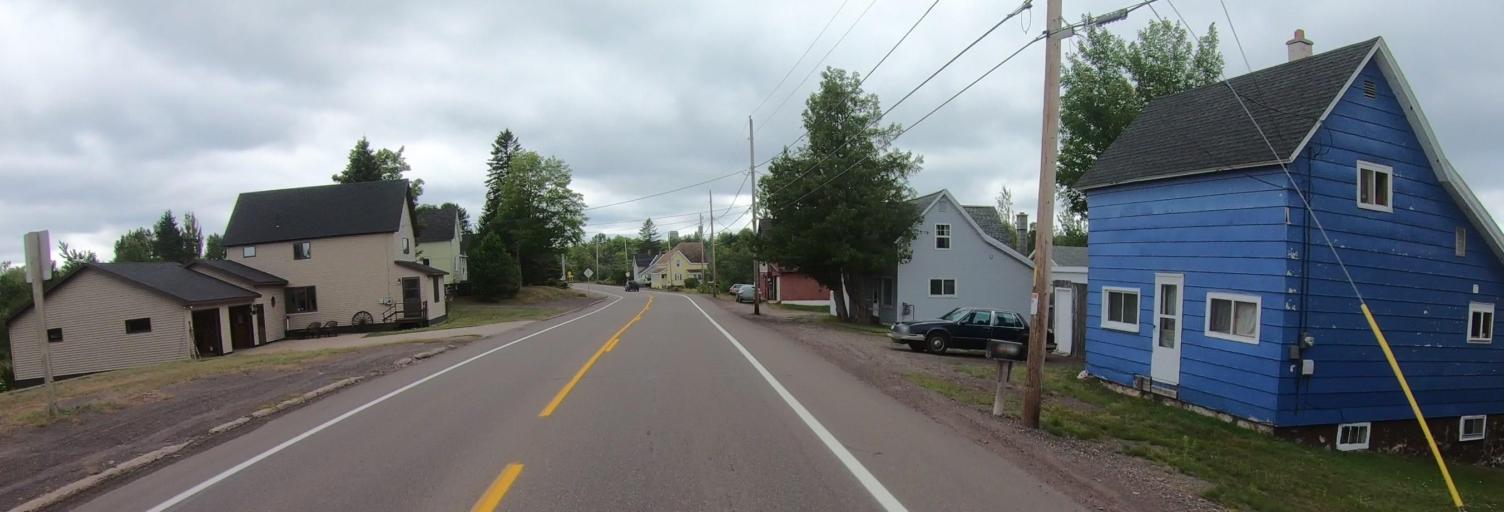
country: US
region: Michigan
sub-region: Houghton County
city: Laurium
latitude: 47.2696
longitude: -88.4203
